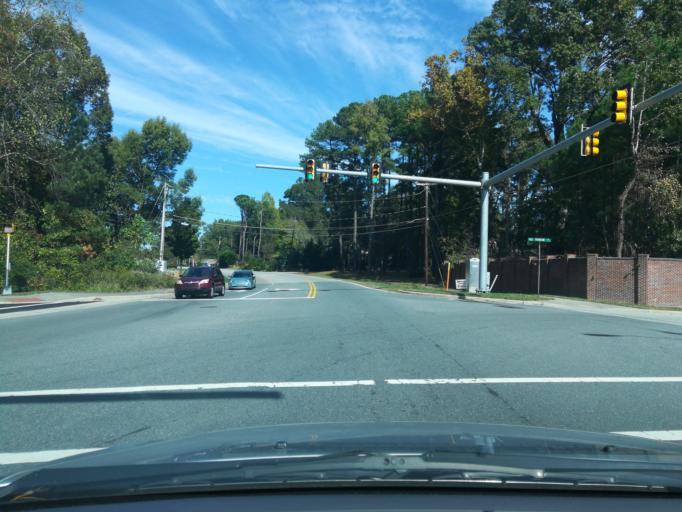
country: US
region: North Carolina
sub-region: Durham County
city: Durham
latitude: 35.9650
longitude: -78.9763
